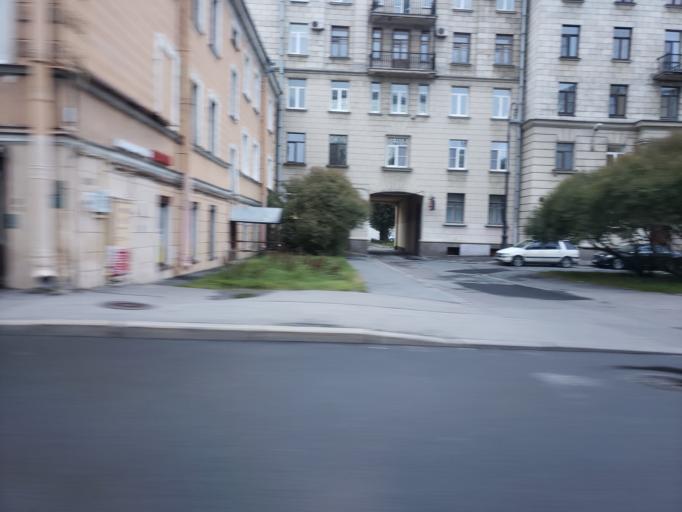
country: RU
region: St.-Petersburg
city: Vasyl'evsky Ostrov
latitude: 59.9317
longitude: 30.2578
